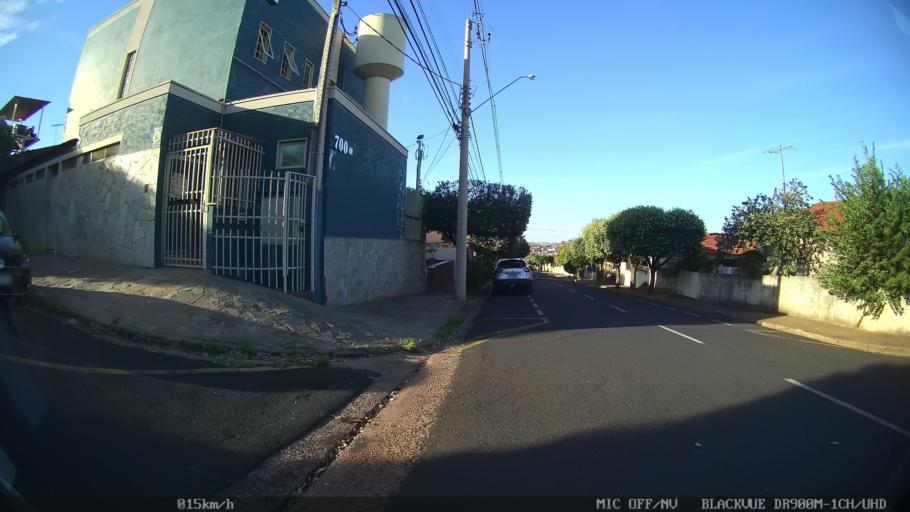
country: BR
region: Sao Paulo
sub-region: Sao Jose Do Rio Preto
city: Sao Jose do Rio Preto
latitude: -20.8295
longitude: -49.3715
